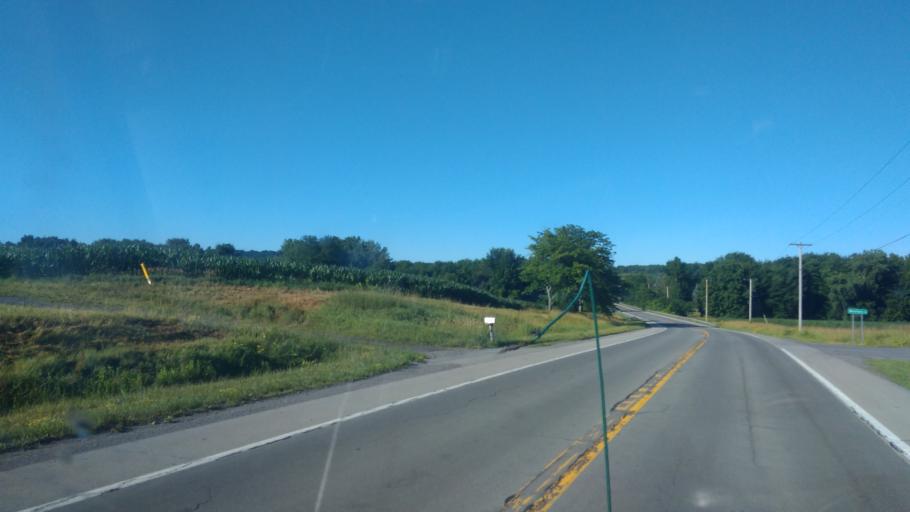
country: US
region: New York
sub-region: Wayne County
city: Sodus
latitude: 43.1874
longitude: -77.0759
